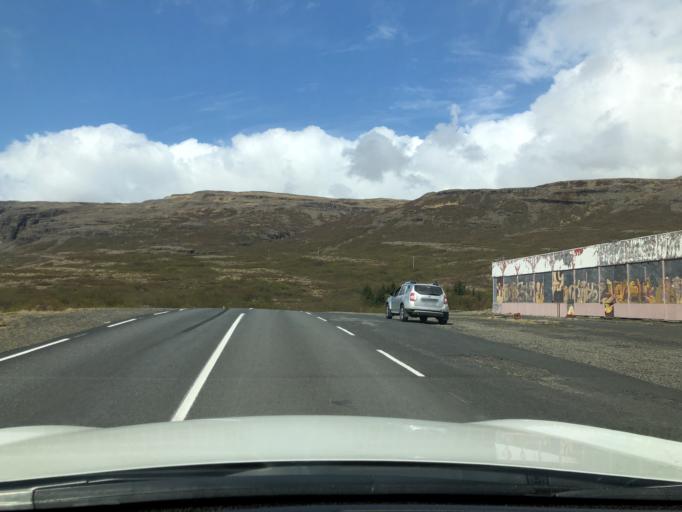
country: IS
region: South
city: Hveragerdi
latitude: 64.3850
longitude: -21.3417
